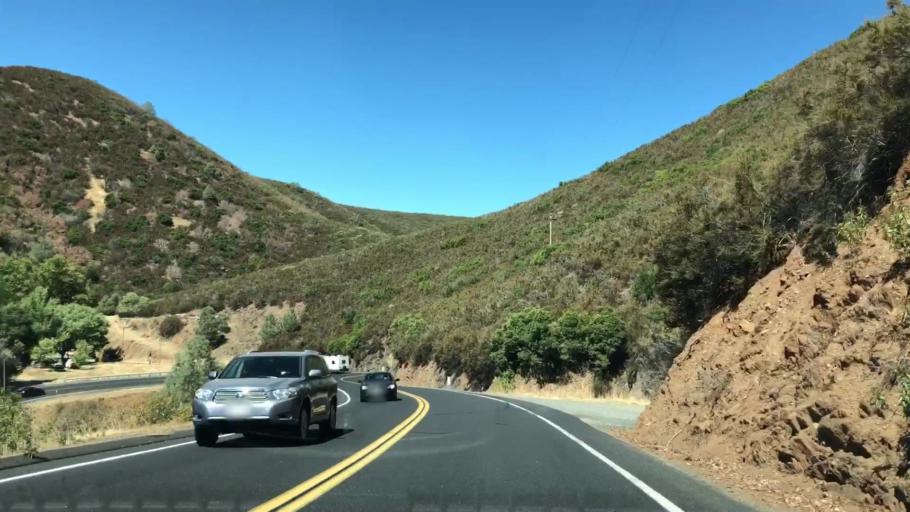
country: US
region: California
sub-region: Tuolumne County
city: Tuolumne City
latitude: 37.8243
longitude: -120.2829
